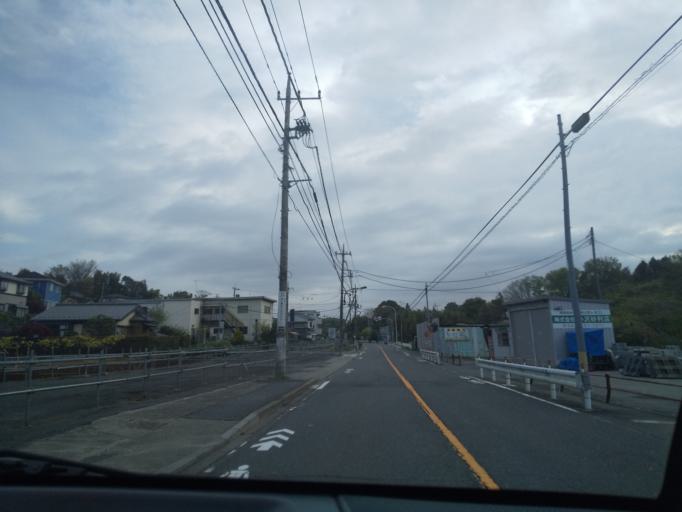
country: JP
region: Tokyo
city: Chofugaoka
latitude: 35.6224
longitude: 139.4806
